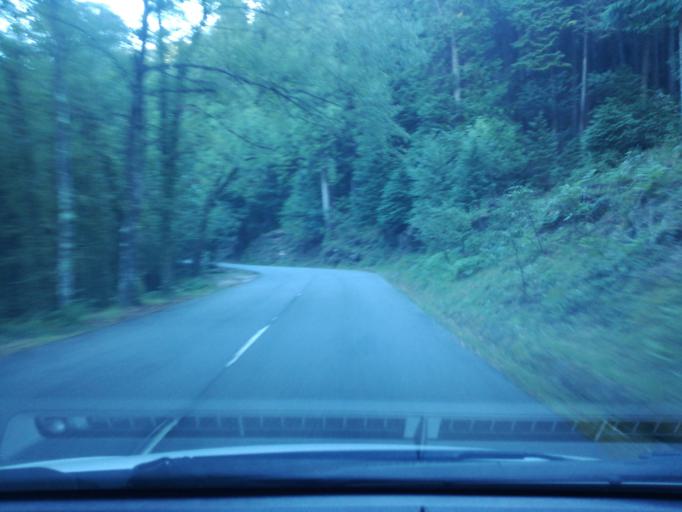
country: PT
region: Braga
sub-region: Vieira do Minho
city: Real
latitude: 41.7481
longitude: -8.1536
